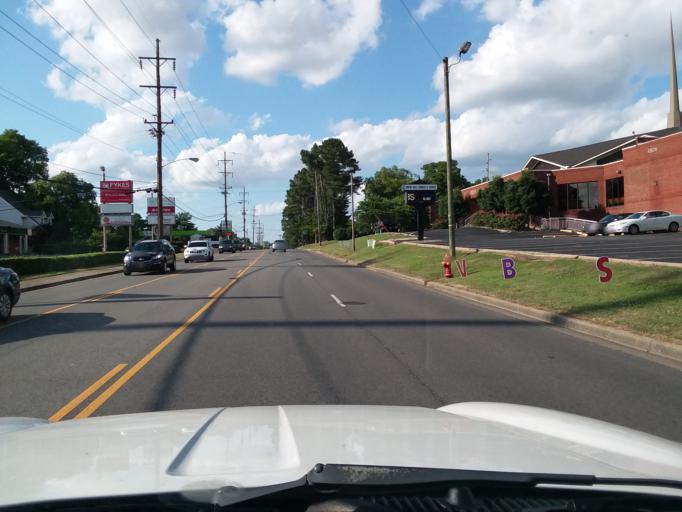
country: US
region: Tennessee
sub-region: Davidson County
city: Oak Hill
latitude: 36.0761
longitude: -86.7590
